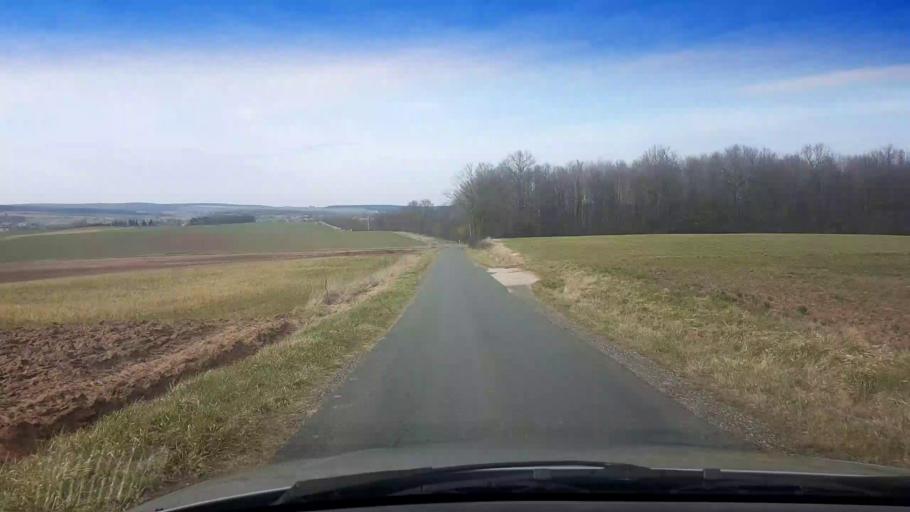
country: DE
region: Bavaria
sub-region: Upper Franconia
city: Burgebrach
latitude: 49.8101
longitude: 10.7599
